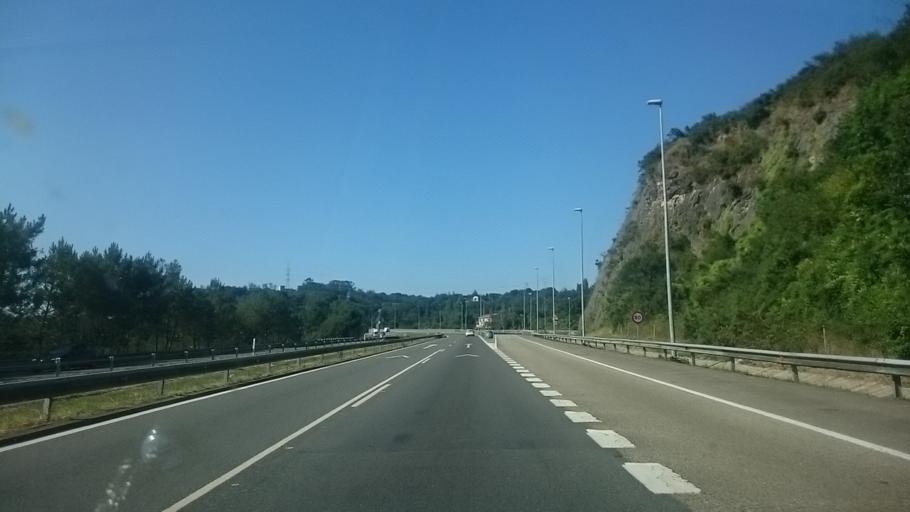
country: ES
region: Asturias
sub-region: Province of Asturias
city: Castandiello
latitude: 43.3135
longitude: -5.8680
